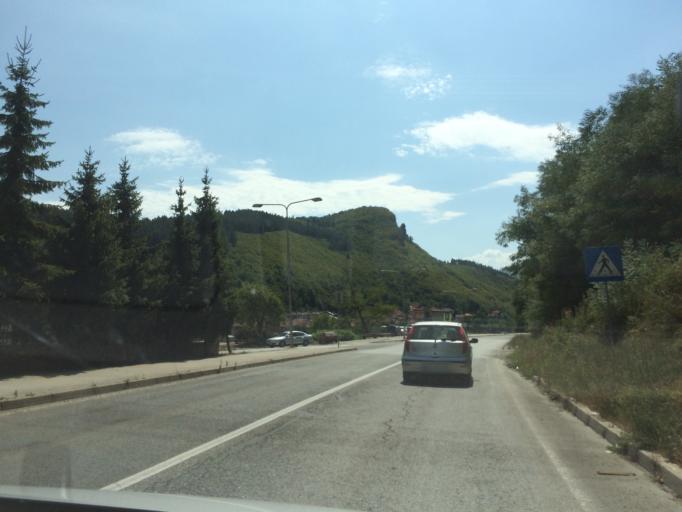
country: RS
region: Central Serbia
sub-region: Zlatiborski Okrug
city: Prijepolje
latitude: 43.3873
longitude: 19.6415
